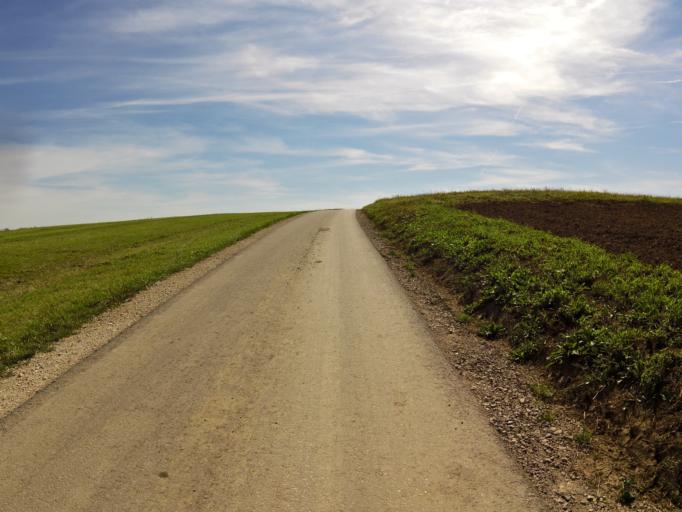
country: DE
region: Baden-Wuerttemberg
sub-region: Freiburg Region
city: Donaueschingen
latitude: 47.9851
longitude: 8.5062
